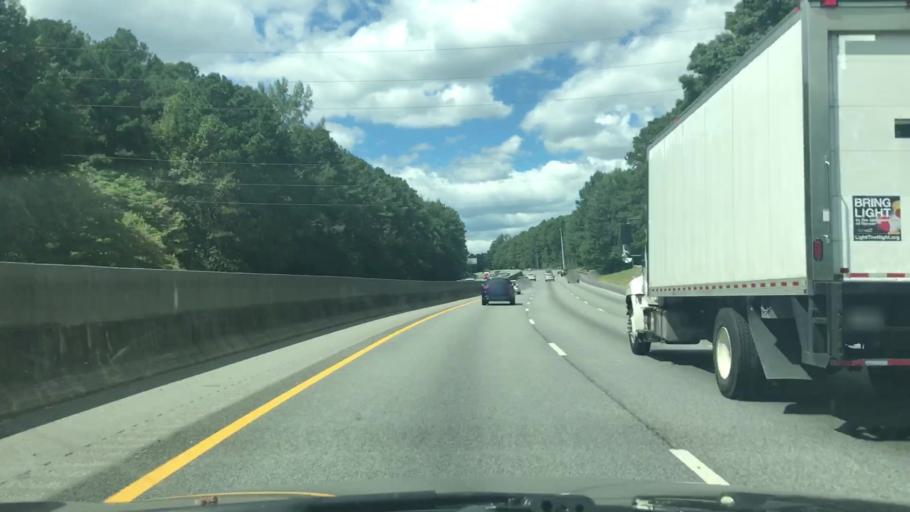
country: US
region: Georgia
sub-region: DeKalb County
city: Stone Mountain
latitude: 33.8227
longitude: -84.1719
